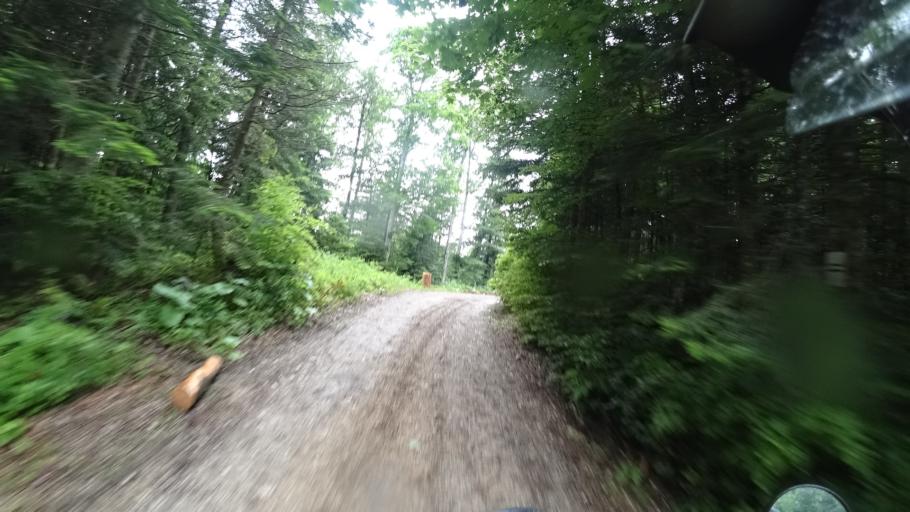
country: HR
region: Primorsko-Goranska
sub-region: Grad Delnice
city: Delnice
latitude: 45.3108
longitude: 14.9230
